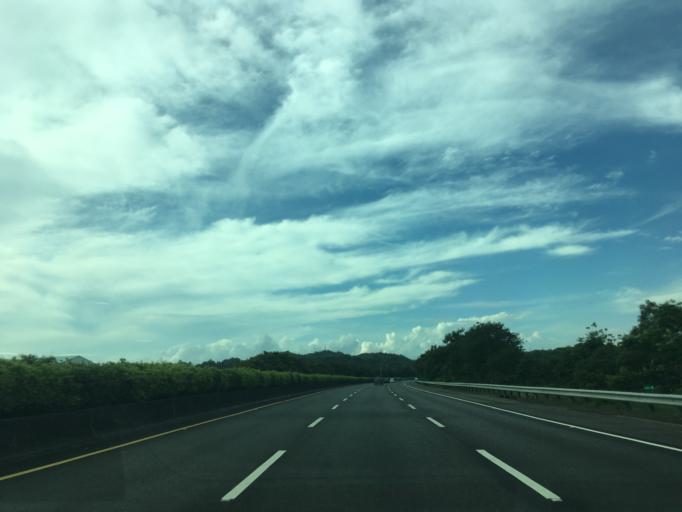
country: TW
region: Taiwan
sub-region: Chiayi
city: Jiayi Shi
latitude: 23.5160
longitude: 120.4851
